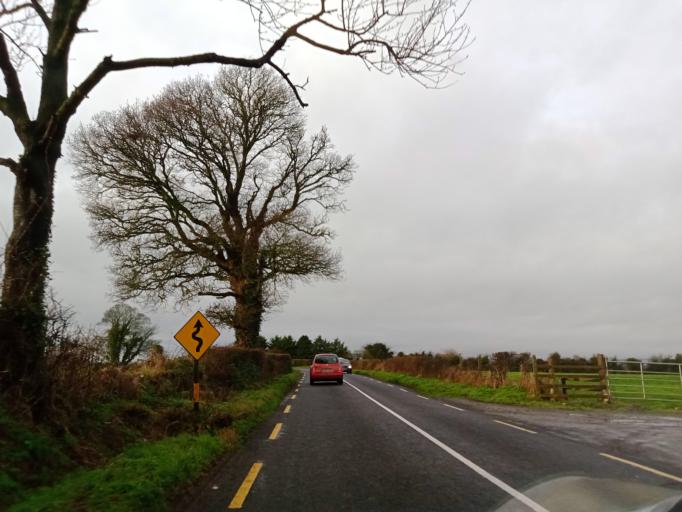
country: IE
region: Leinster
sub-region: Kilkenny
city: Callan
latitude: 52.5741
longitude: -7.3960
